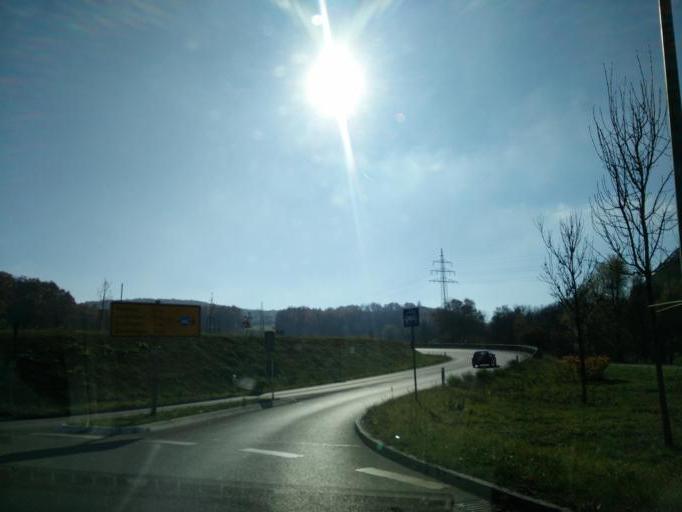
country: DE
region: Baden-Wuerttemberg
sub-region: Tuebingen Region
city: Dusslingen
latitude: 48.4876
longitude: 9.0681
